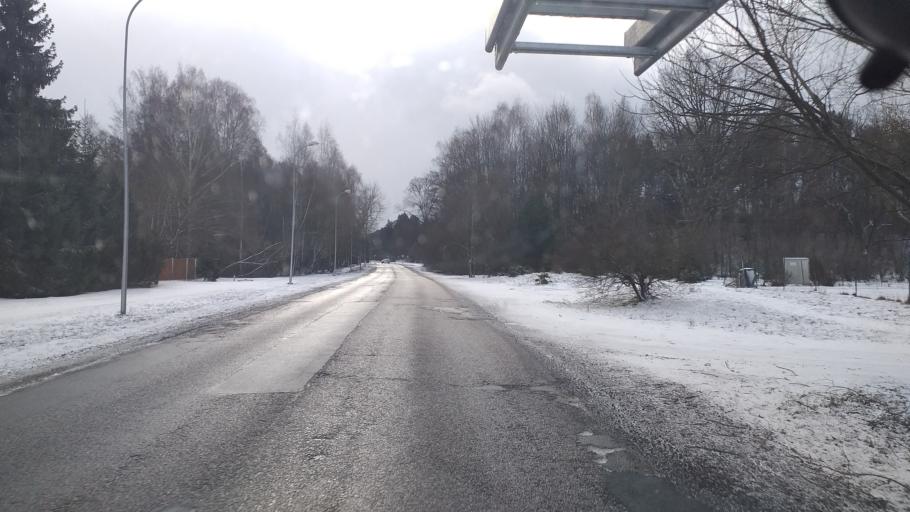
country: LV
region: Riga
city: Bolderaja
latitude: 56.9860
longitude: 24.0321
